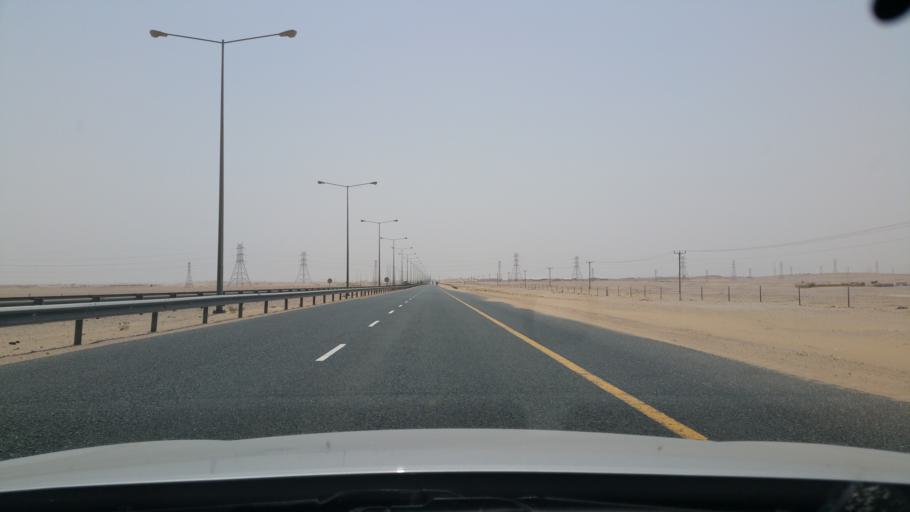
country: QA
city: Umm Bab
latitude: 24.9658
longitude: 50.9595
